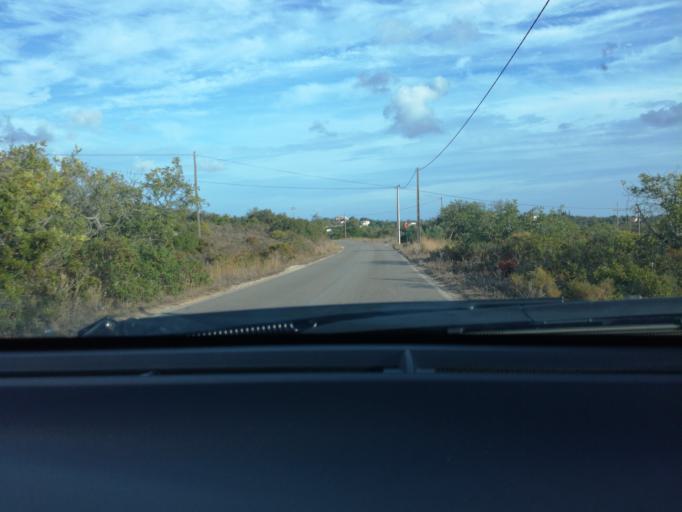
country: PT
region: Faro
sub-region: Olhao
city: Laranjeiro
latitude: 37.0784
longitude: -7.8267
